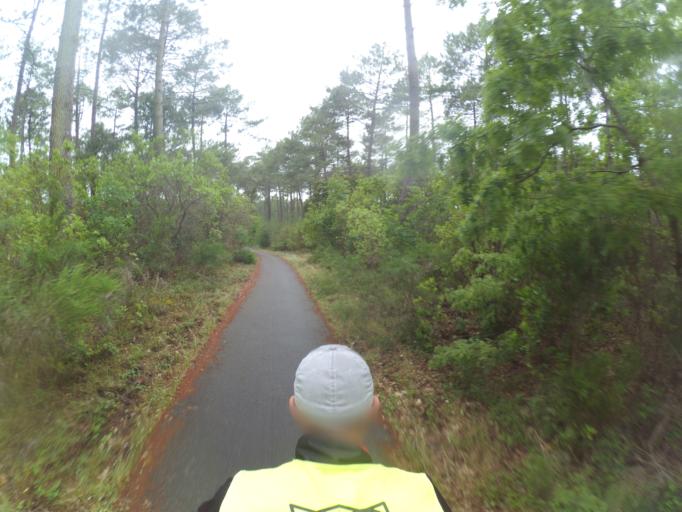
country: FR
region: Aquitaine
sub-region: Departement des Landes
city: Mimizan
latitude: 44.2218
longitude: -1.2516
